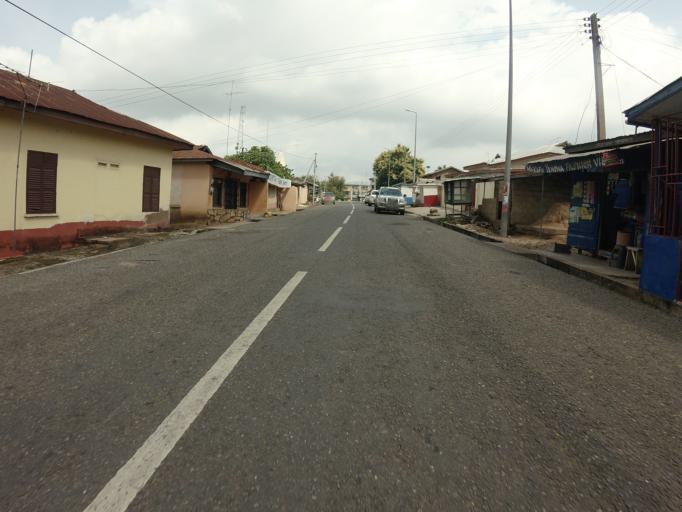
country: GH
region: Volta
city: Ho
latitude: 6.6128
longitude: 0.4684
